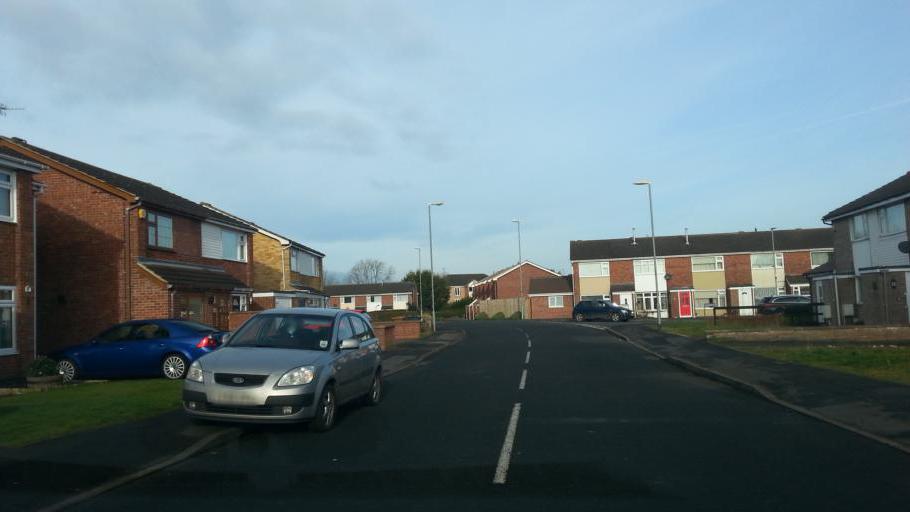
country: GB
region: England
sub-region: Leicestershire
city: Melton Mowbray
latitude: 52.7589
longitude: -0.8958
